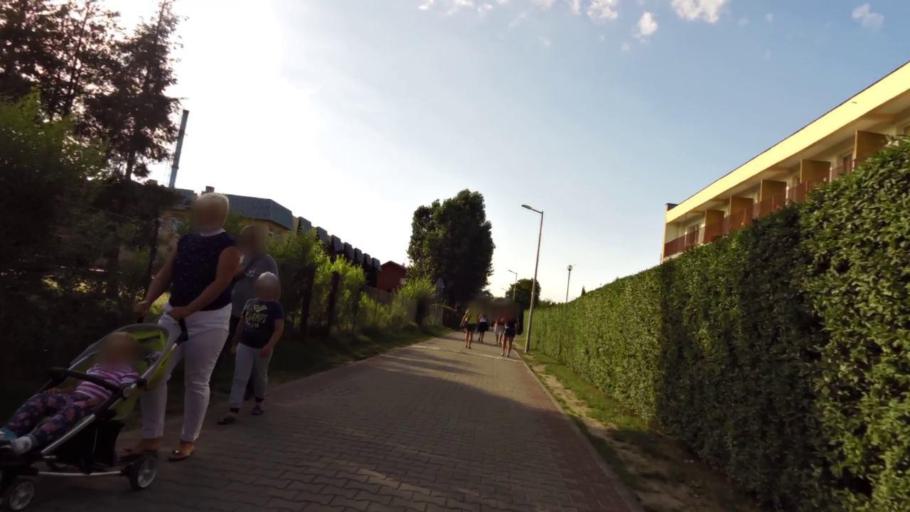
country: PL
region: West Pomeranian Voivodeship
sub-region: Powiat slawienski
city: Darlowo
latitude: 54.3787
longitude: 16.3156
